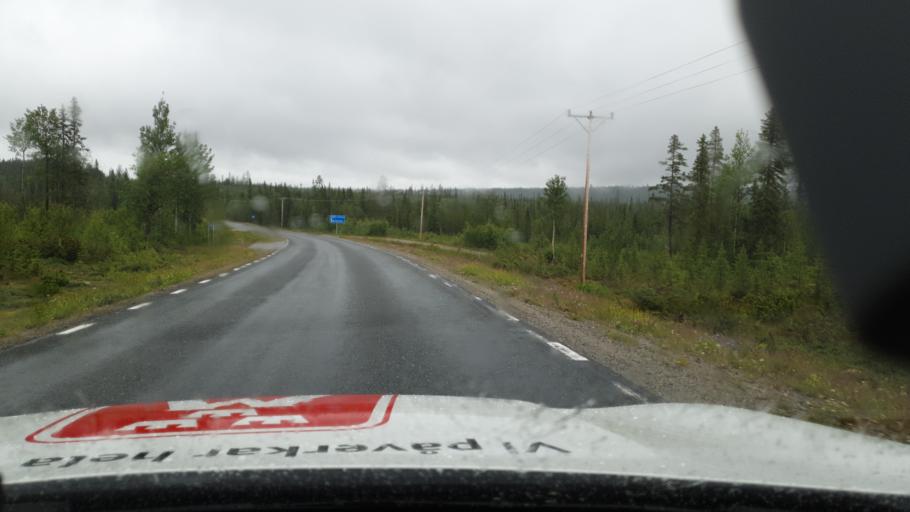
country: SE
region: Vaesterbotten
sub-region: Lycksele Kommun
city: Soderfors
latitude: 64.3859
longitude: 18.0024
